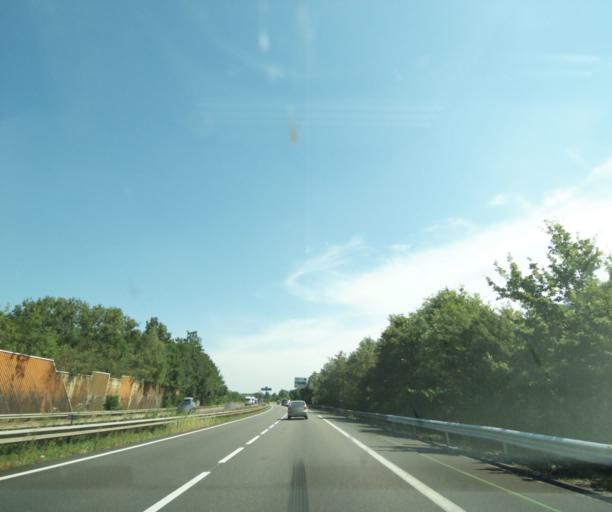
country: FR
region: Lorraine
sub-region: Departement de Meurthe-et-Moselle
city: Dommartin-les-Toul
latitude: 48.6720
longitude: 5.9192
